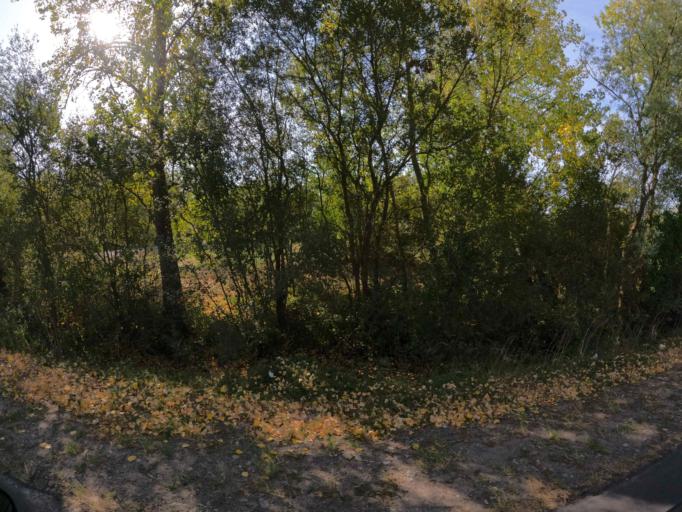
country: FR
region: Pays de la Loire
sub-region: Departement de la Vendee
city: Le Perrier
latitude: 46.8109
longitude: -2.0125
